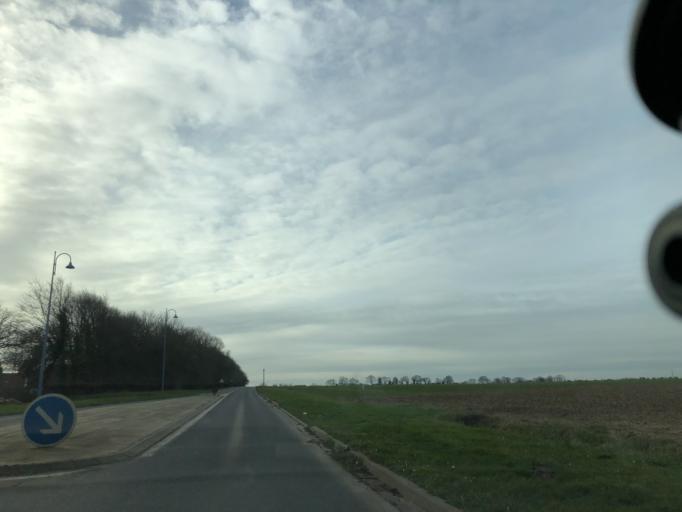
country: FR
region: Lower Normandy
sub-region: Departement du Calvados
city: Hermanville-sur-Mer
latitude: 49.2887
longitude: -0.3194
